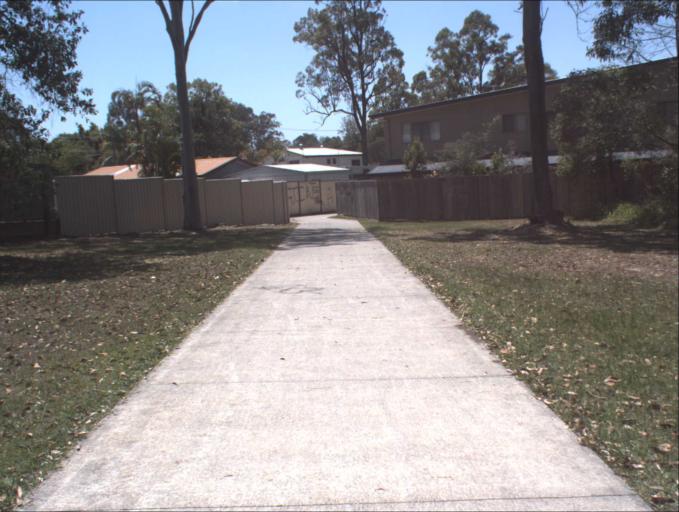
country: AU
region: Queensland
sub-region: Logan
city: Beenleigh
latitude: -27.6984
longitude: 153.2093
